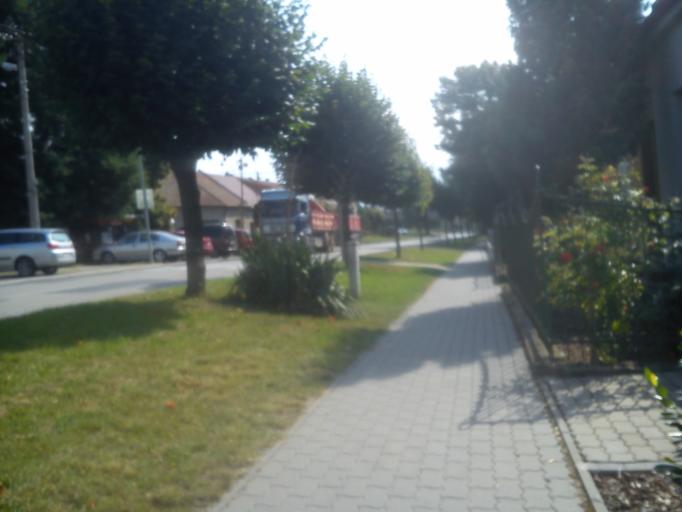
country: CZ
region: South Moravian
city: Sokolnice
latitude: 49.1057
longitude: 16.7521
